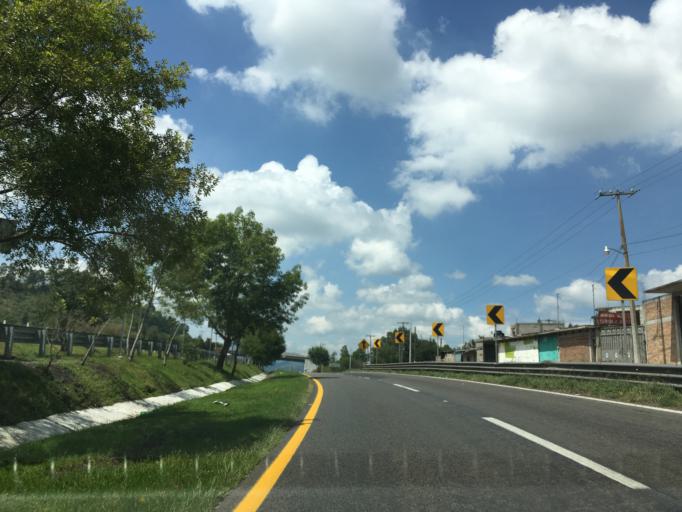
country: MX
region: Michoacan
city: Lagunillas
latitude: 19.5588
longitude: -101.4178
